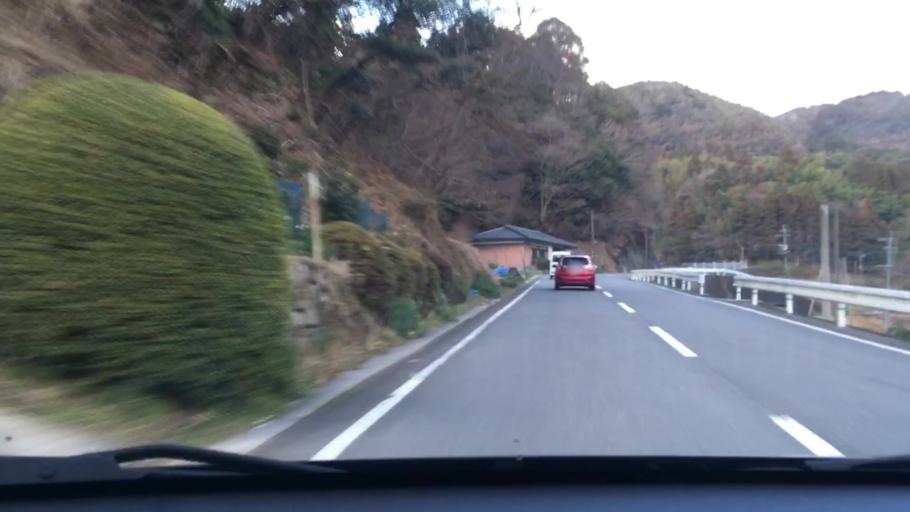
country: JP
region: Oita
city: Bungo-Takada-shi
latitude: 33.4655
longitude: 131.3882
